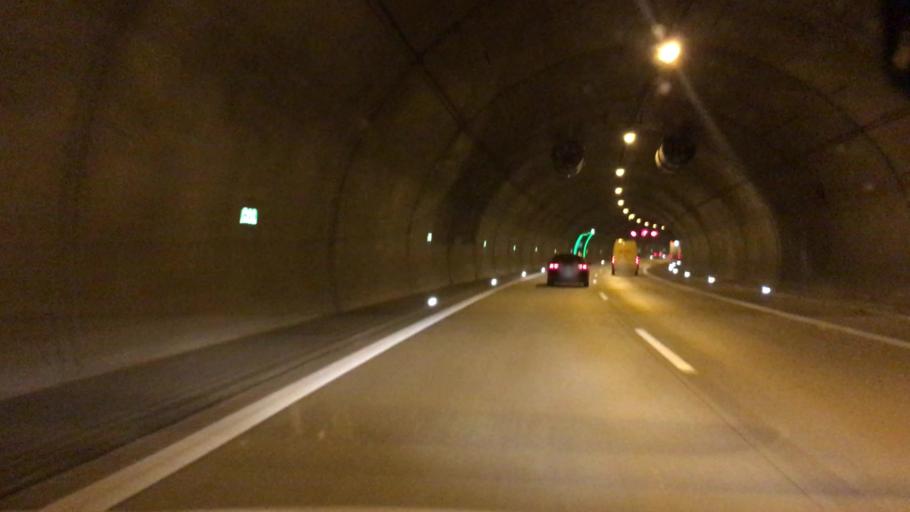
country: DE
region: Saxony
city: Freital
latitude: 51.0260
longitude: 13.6816
